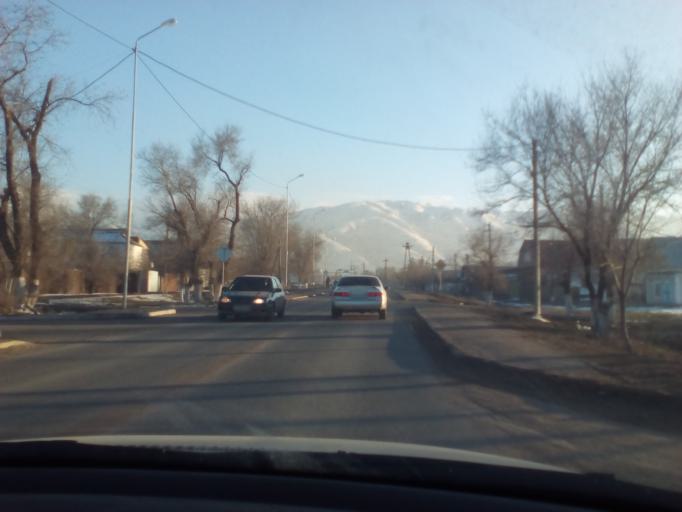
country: KZ
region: Almaty Oblysy
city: Burunday
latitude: 43.1821
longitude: 76.4144
